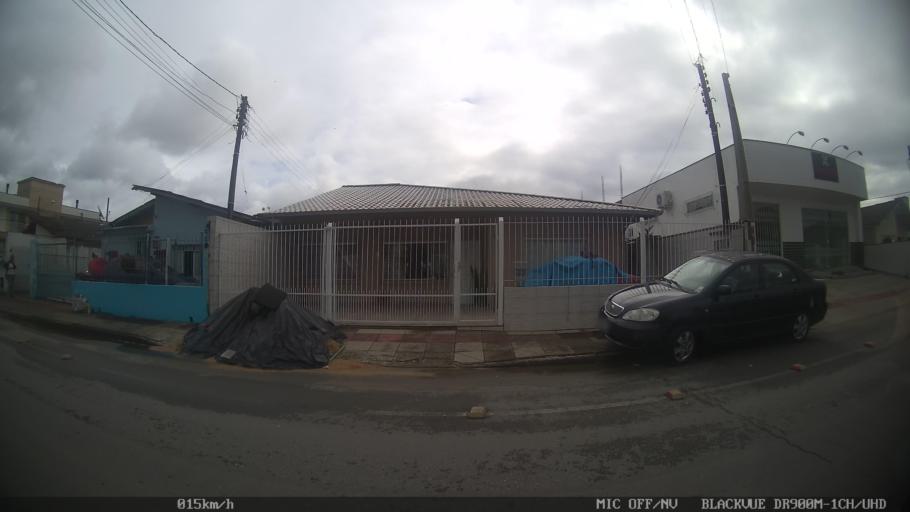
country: BR
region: Santa Catarina
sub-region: Biguacu
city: Biguacu
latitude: -27.5146
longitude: -48.6452
